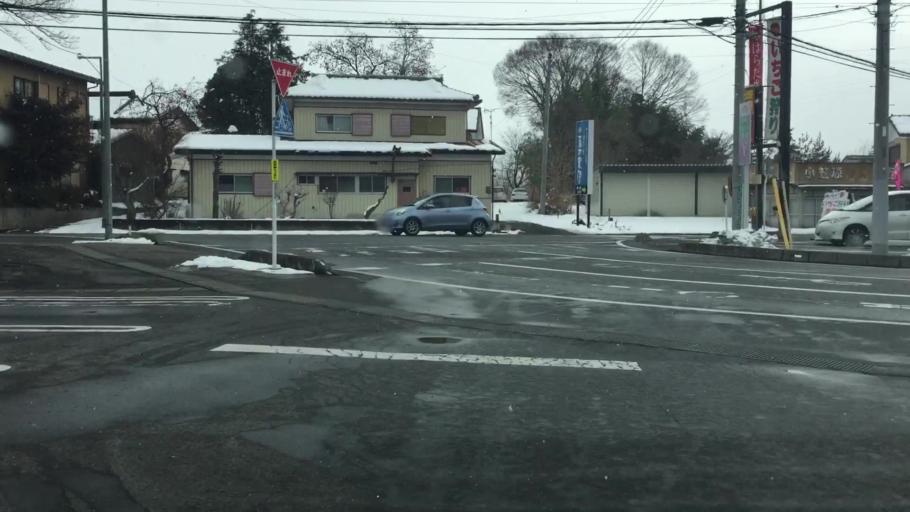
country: JP
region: Gunma
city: Numata
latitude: 36.6600
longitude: 139.0780
